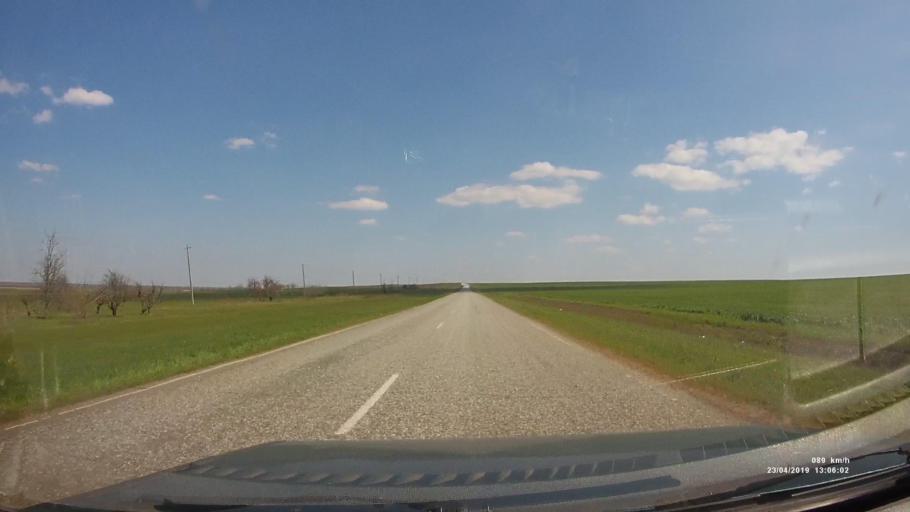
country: RU
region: Kalmykiya
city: Yashalta
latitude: 46.5918
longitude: 42.7337
